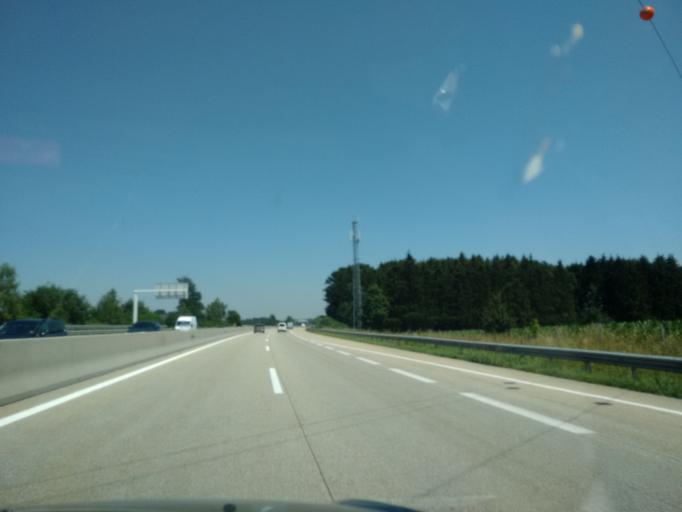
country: AT
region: Upper Austria
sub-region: Wels-Land
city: Sattledt
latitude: 48.0456
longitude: 14.0012
